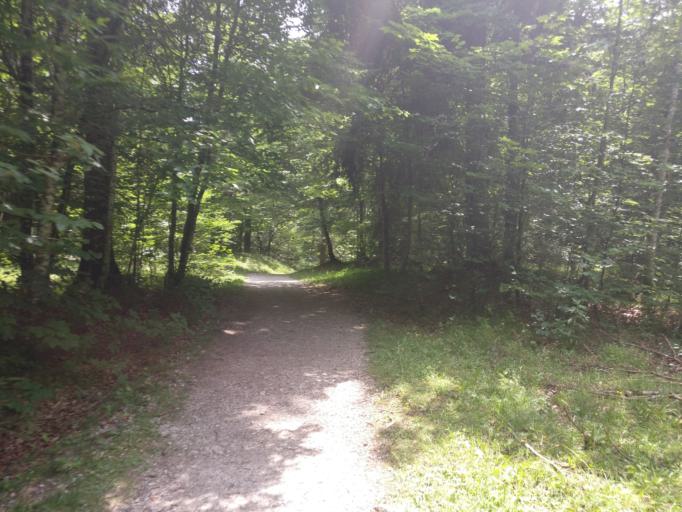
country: AT
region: Salzburg
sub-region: Politischer Bezirk Zell am See
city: Sankt Martin bei Lofer
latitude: 47.5362
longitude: 12.7198
